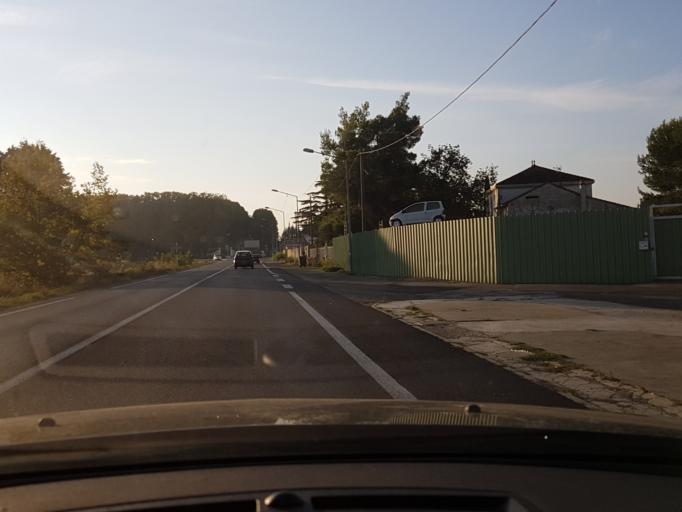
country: FR
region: Provence-Alpes-Cote d'Azur
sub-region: Departement des Bouches-du-Rhone
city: Saint-Andiol
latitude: 43.8401
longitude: 4.9387
